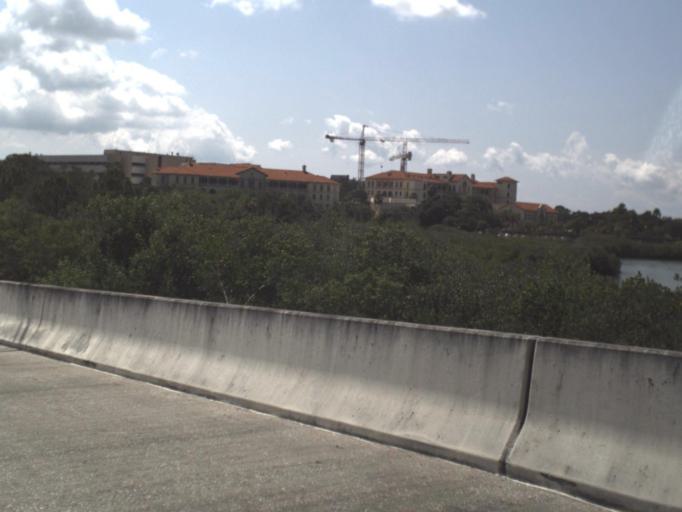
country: US
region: Florida
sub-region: Pinellas County
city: Bay Pines
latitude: 27.8139
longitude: -82.7837
